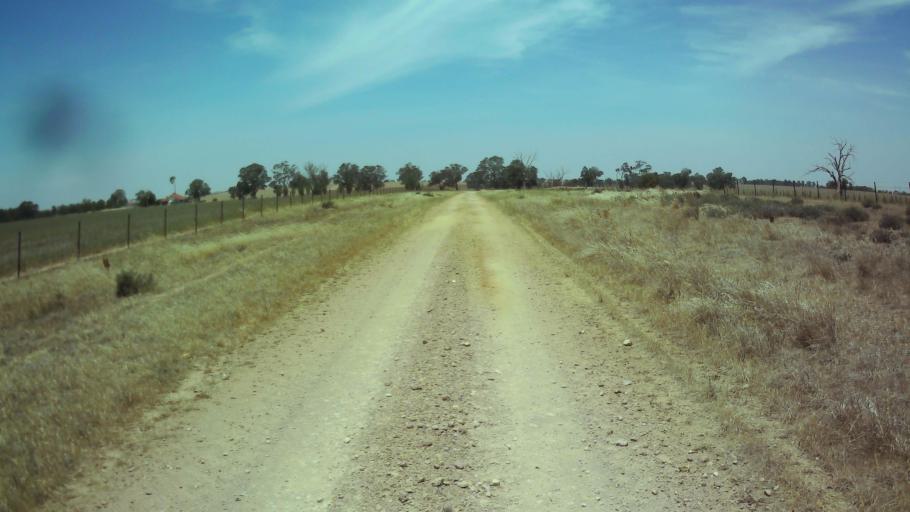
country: AU
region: New South Wales
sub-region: Weddin
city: Grenfell
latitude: -34.0021
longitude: 148.3977
